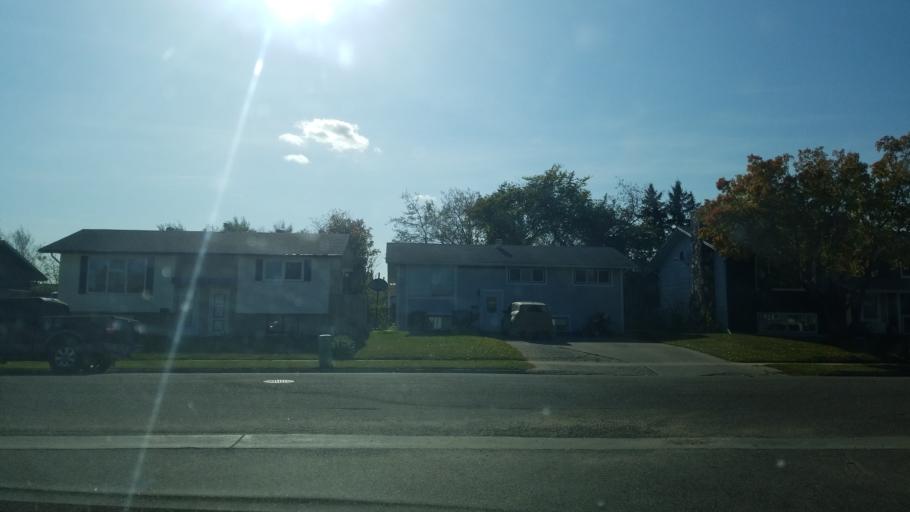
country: CA
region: Saskatchewan
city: Lloydminster
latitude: 53.2676
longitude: -110.0137
